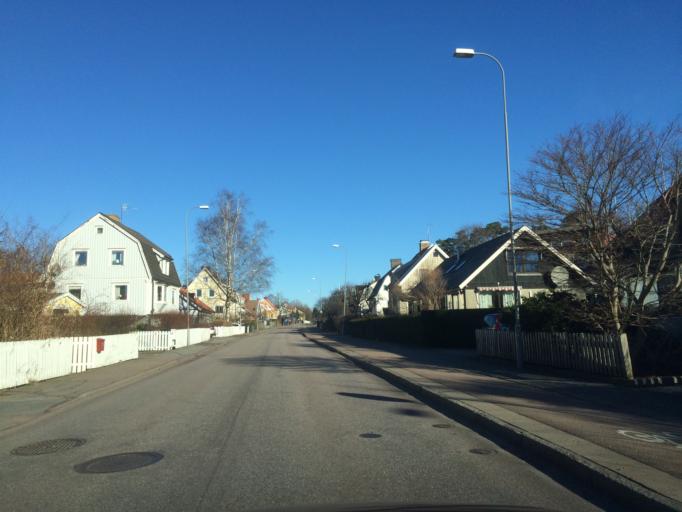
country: SE
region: Vaestra Goetaland
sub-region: Goteborg
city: Majorna
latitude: 57.6710
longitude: 11.8971
